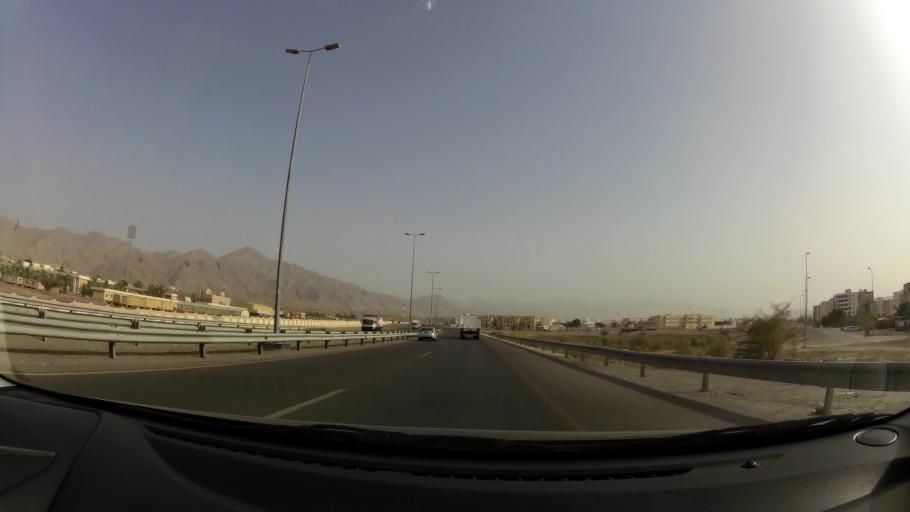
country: OM
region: Muhafazat Masqat
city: Bawshar
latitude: 23.5500
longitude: 58.3665
